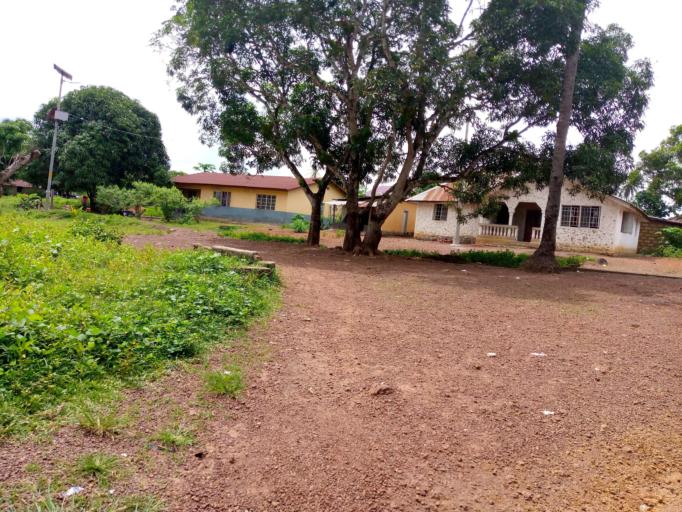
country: SL
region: Southern Province
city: Moyamba
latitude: 8.1541
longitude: -12.4327
